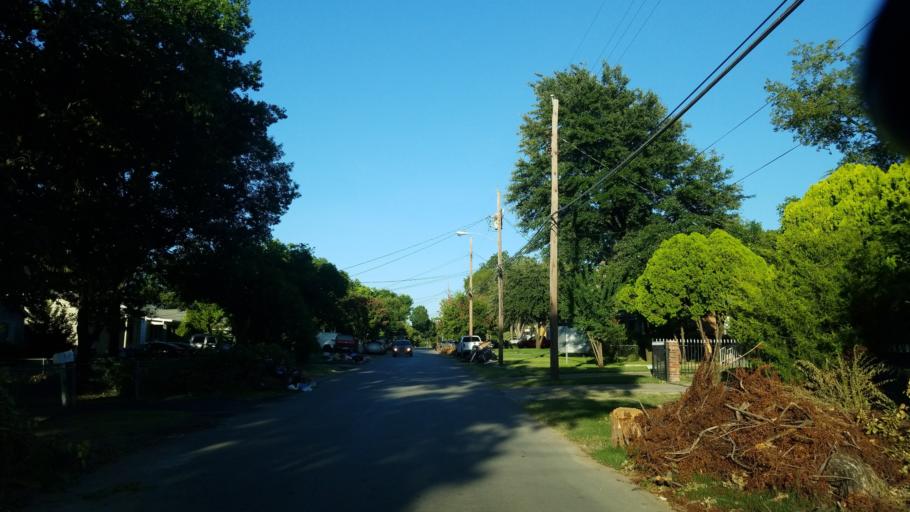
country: US
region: Texas
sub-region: Dallas County
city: Balch Springs
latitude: 32.7769
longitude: -96.6988
